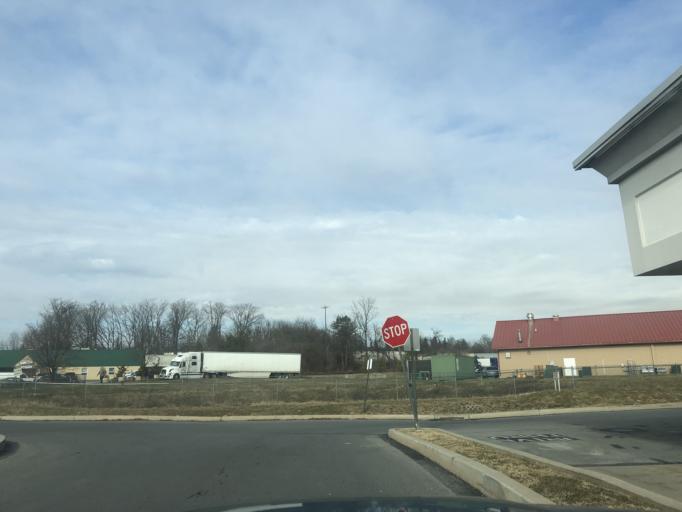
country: US
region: Pennsylvania
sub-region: Lehigh County
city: Ancient Oaks
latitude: 40.5923
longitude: -75.5903
